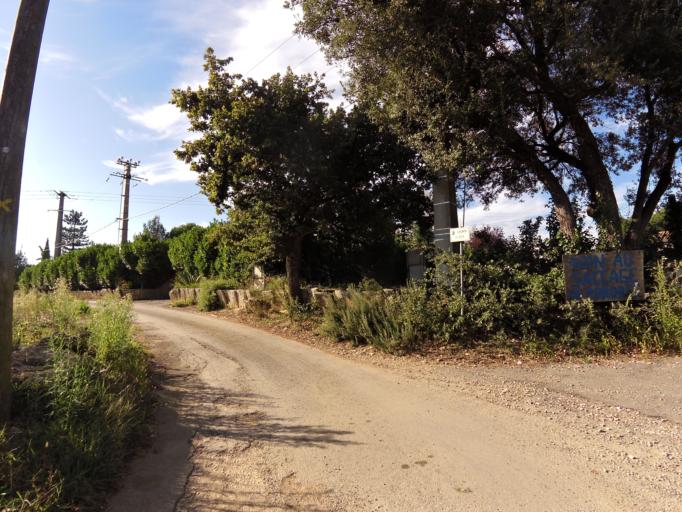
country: FR
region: Languedoc-Roussillon
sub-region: Departement du Gard
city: Villevieille
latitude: 43.8104
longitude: 4.0878
